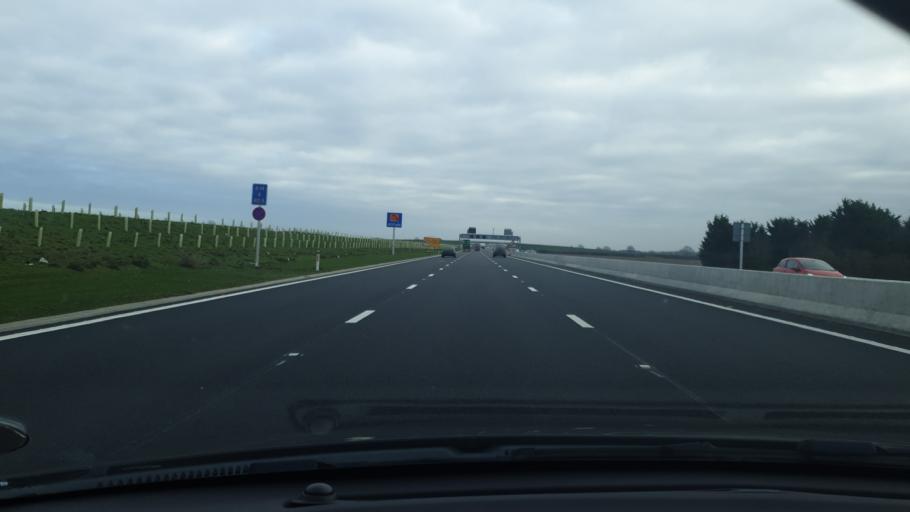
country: GB
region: England
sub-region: Cambridgeshire
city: Hemingford Grey
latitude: 52.2904
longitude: -0.0838
